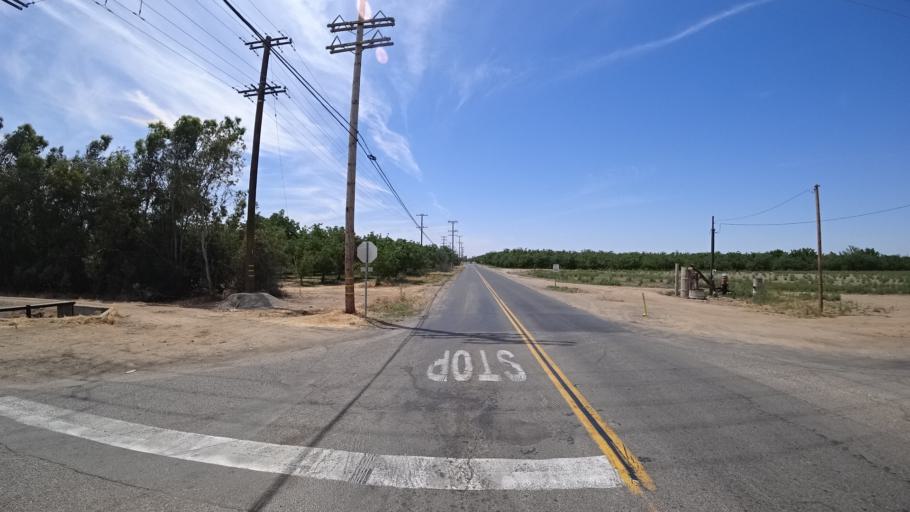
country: US
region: California
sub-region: Kings County
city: Armona
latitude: 36.3425
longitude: -119.6910
